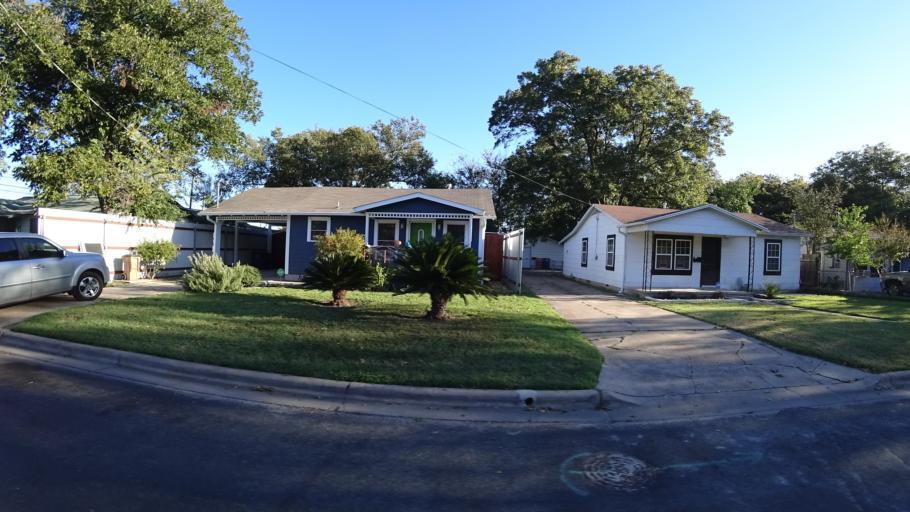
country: US
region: Texas
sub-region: Travis County
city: Austin
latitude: 30.2247
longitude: -97.7700
